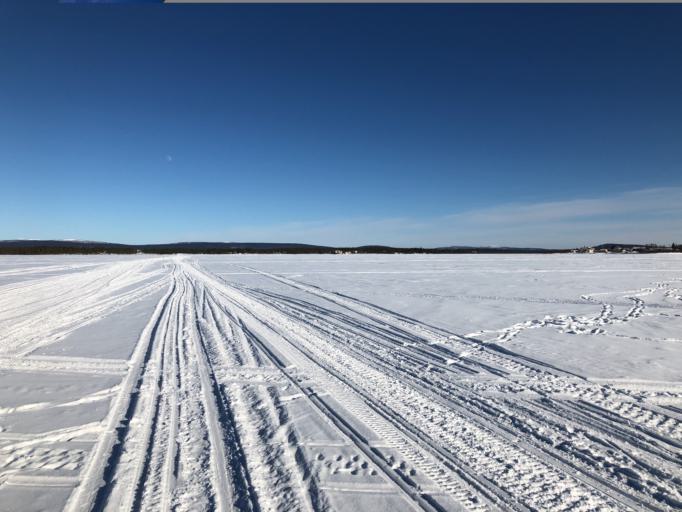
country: SE
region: Norrbotten
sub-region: Kiruna Kommun
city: Kiruna
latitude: 67.8457
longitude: 20.6249
